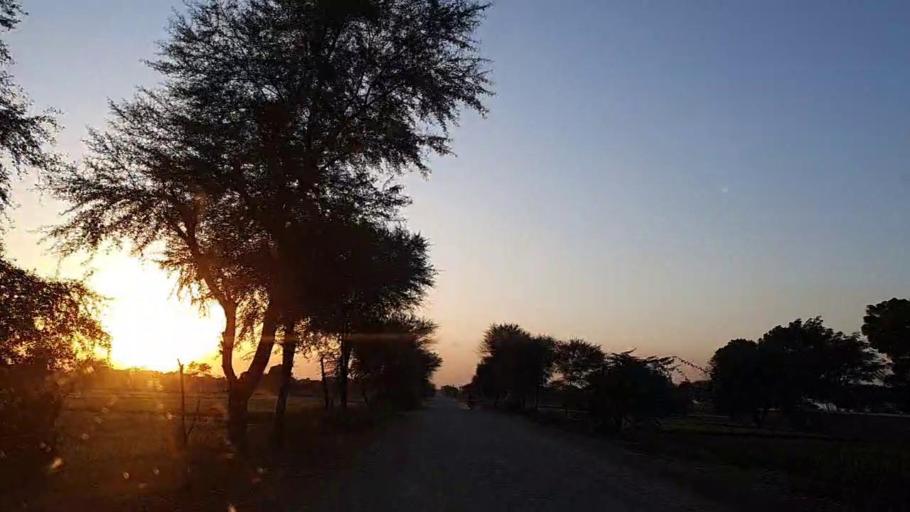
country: PK
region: Sindh
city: Daur
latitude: 26.3503
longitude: 68.3243
